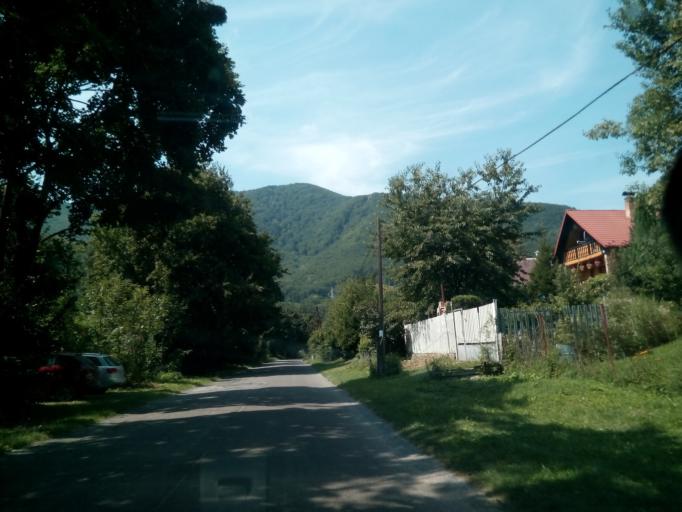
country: SK
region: Presovsky
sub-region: Okres Presov
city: Presov
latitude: 48.8551
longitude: 21.1654
